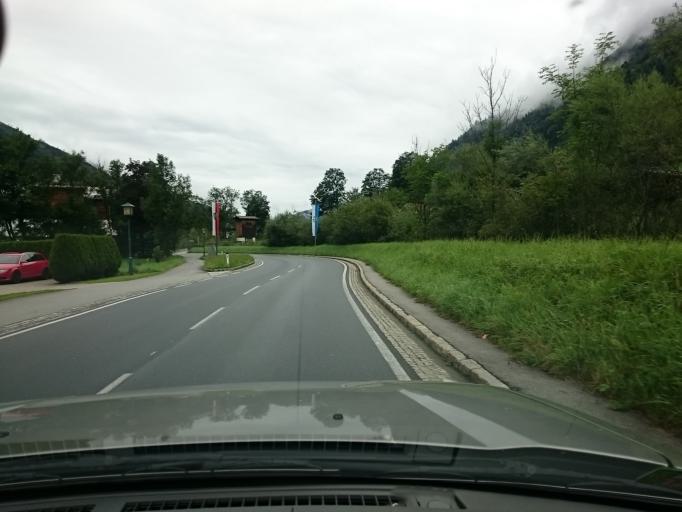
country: AT
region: Salzburg
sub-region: Politischer Bezirk Zell am See
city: Bruck an der Grossglocknerstrasse
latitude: 47.2294
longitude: 12.8270
